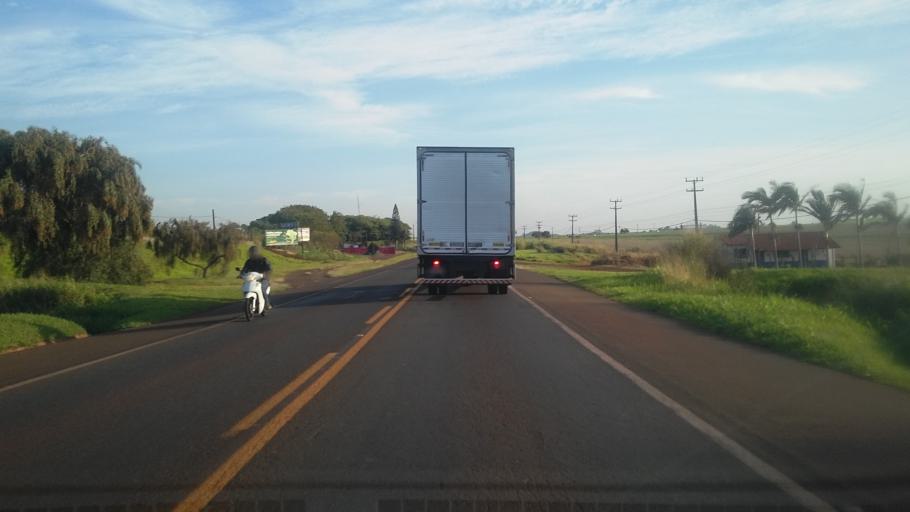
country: BR
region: Parana
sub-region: Bandeirantes
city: Bandeirantes
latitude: -23.1628
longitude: -50.6091
